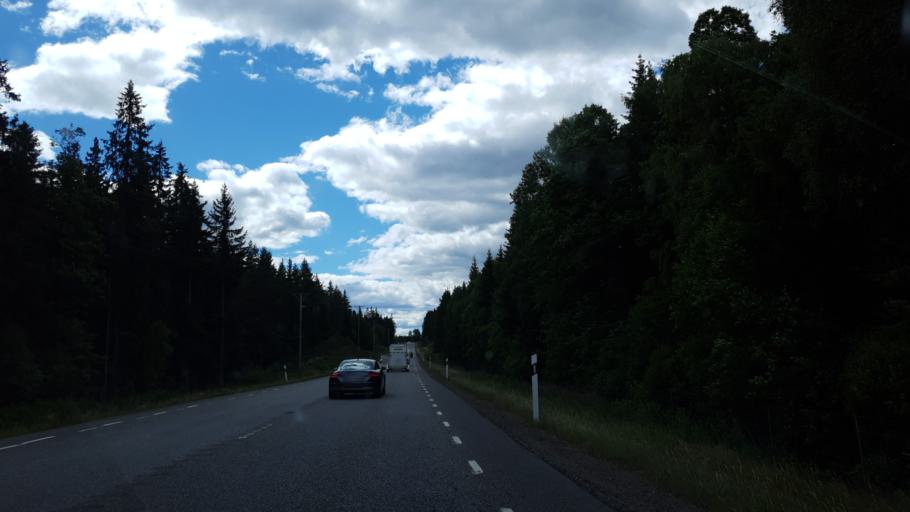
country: SE
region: Kronoberg
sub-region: Vaxjo Kommun
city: Braas
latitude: 57.1745
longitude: 15.1606
